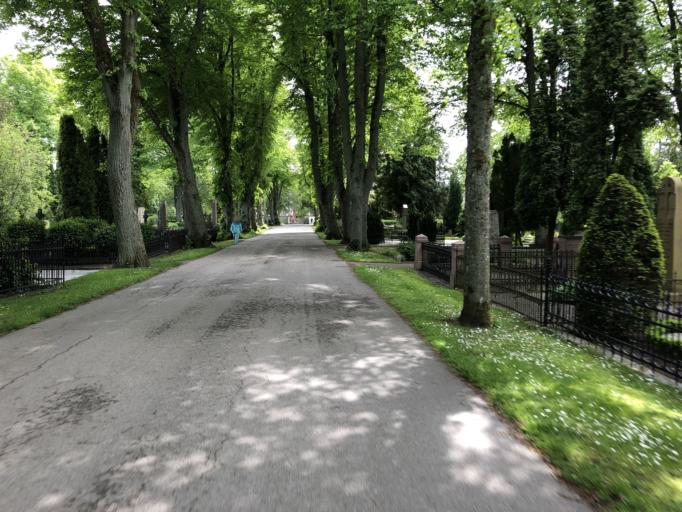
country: SE
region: Skane
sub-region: Lunds Kommun
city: Lund
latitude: 55.7137
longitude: 13.1940
